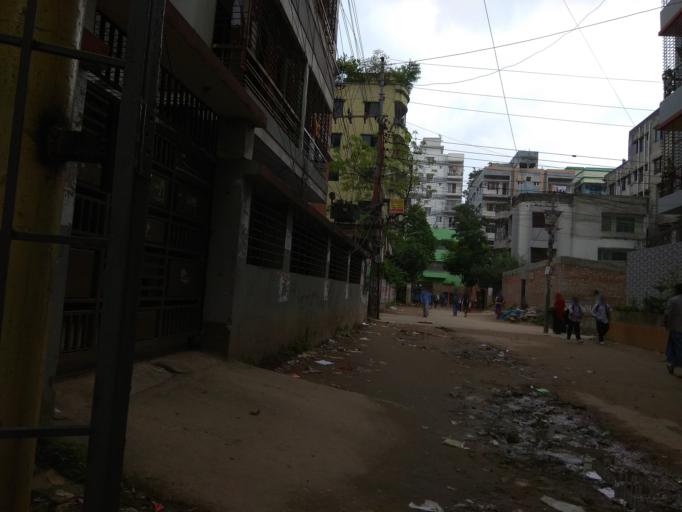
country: BD
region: Dhaka
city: Azimpur
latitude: 23.8135
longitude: 90.3550
